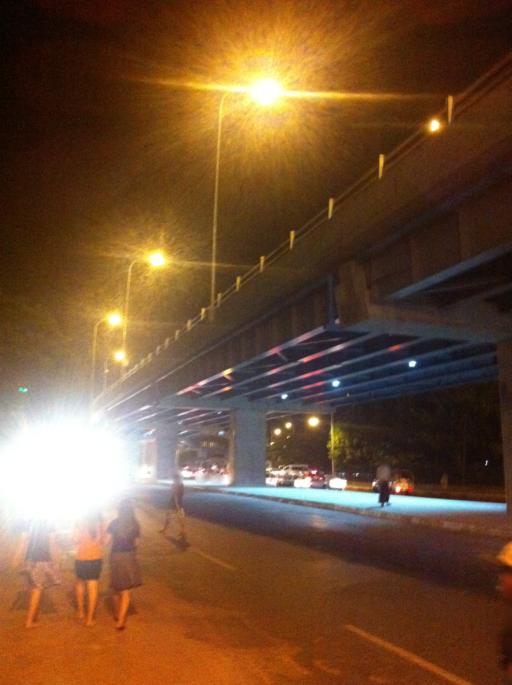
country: MM
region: Yangon
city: Yangon
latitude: 16.8243
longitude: 96.1285
